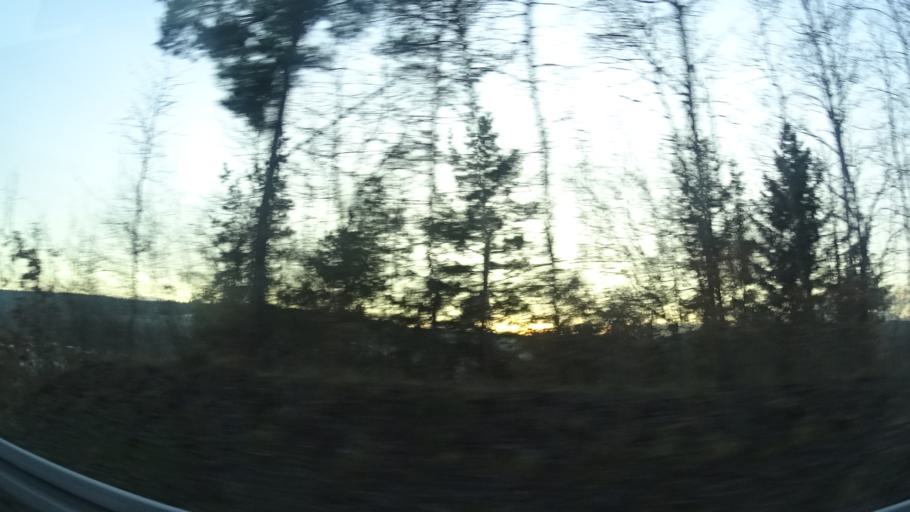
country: DE
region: Bavaria
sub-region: Regierungsbezirk Unterfranken
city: Oberelsbach
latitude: 50.3830
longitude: 10.1091
